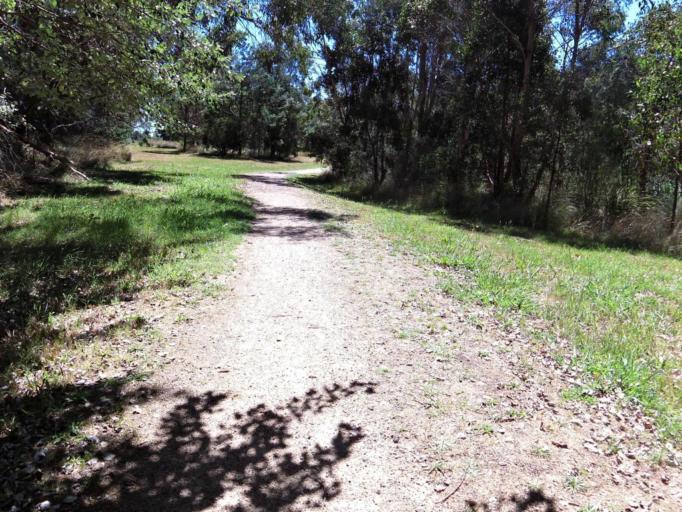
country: AU
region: Victoria
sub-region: Hume
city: Sunbury
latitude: -37.3577
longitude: 144.5349
